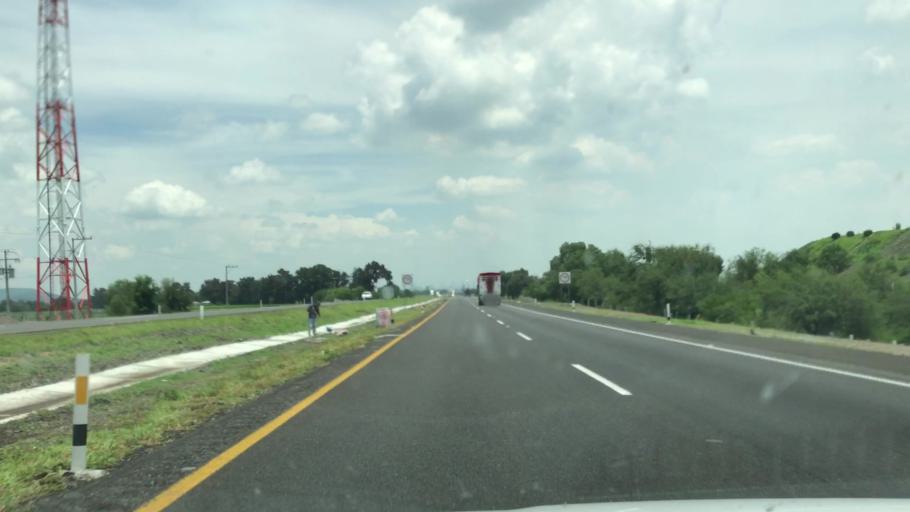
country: MX
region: Guanajuato
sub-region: Salamanca
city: San Vicente de Flores
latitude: 20.6191
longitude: -101.2322
